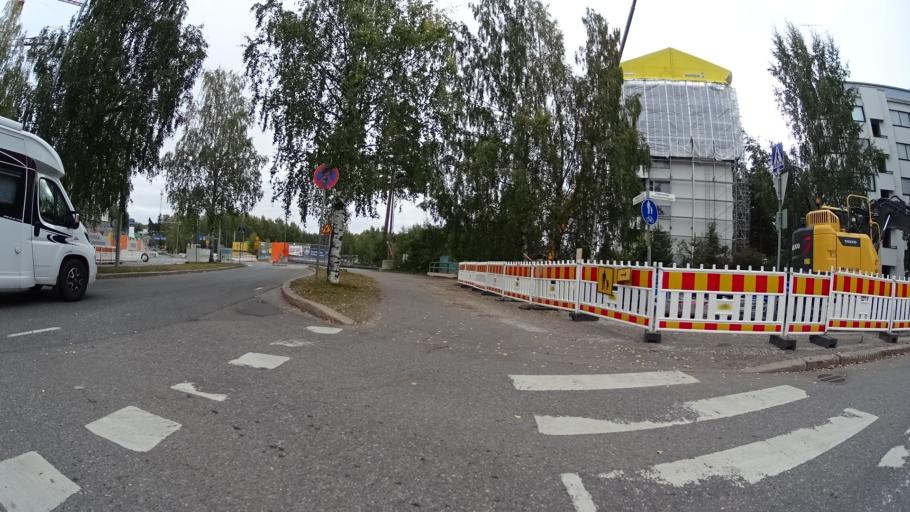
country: FI
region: Uusimaa
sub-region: Helsinki
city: Vantaa
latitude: 60.2232
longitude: 25.0765
